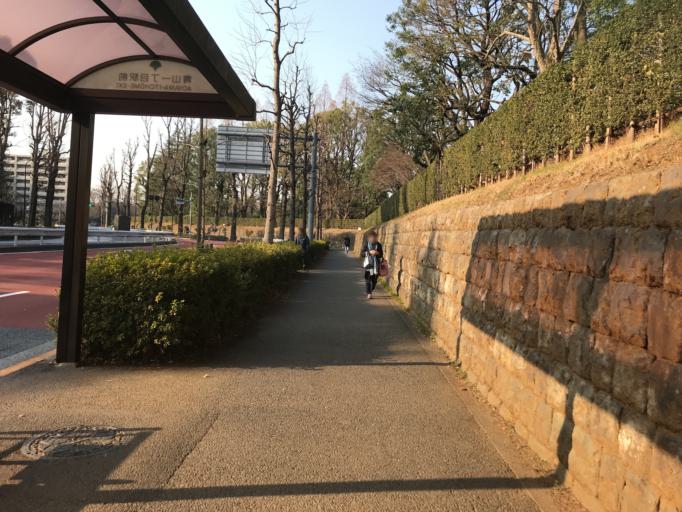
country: JP
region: Tokyo
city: Tokyo
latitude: 35.6739
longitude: 139.7236
